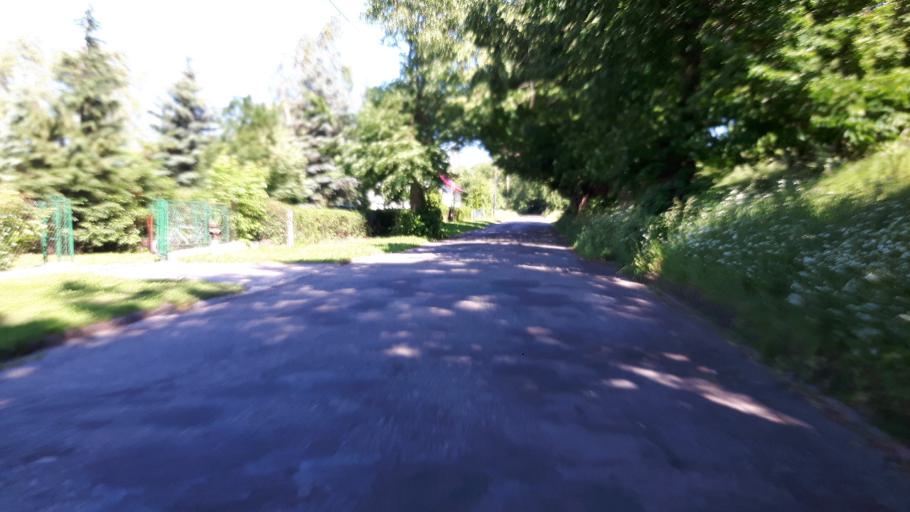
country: PL
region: Pomeranian Voivodeship
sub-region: Powiat slupski
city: Glowczyce
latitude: 54.6782
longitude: 17.4252
